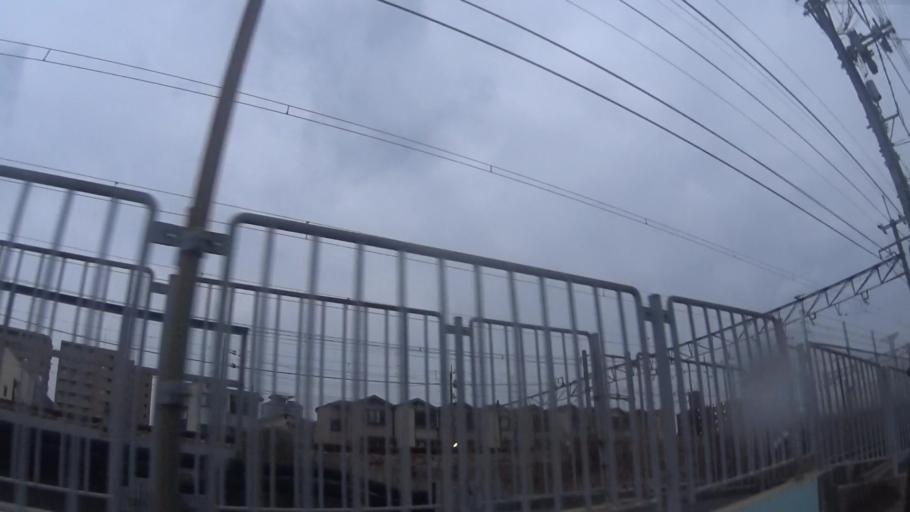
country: JP
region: Kyoto
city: Muko
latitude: 34.9527
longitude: 135.7095
